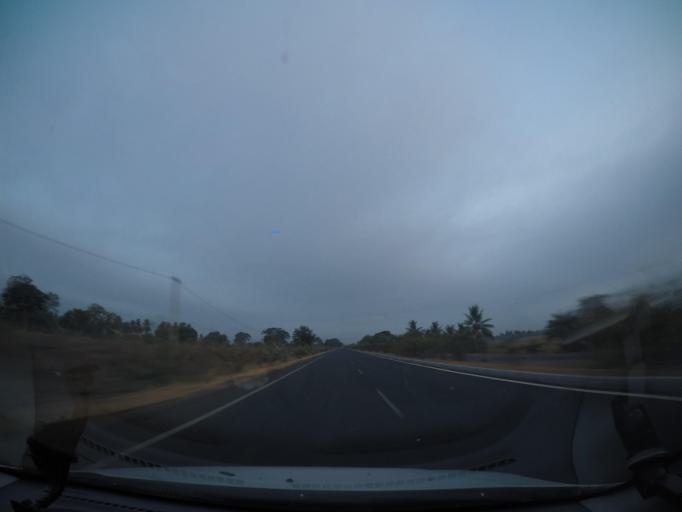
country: IN
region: Andhra Pradesh
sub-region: West Godavari
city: Tadepallegudem
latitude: 16.8098
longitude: 81.3567
